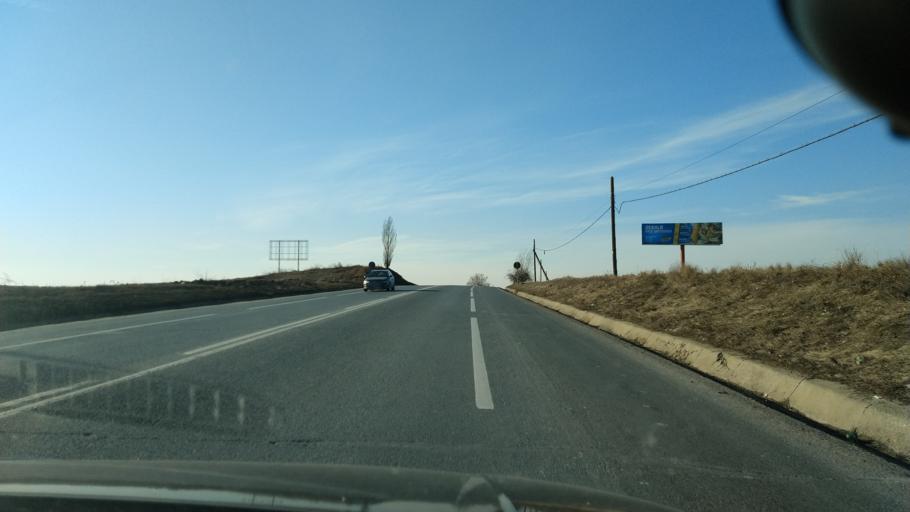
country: RO
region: Iasi
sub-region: Comuna Baltati
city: Baltati
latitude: 47.2206
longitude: 27.1361
